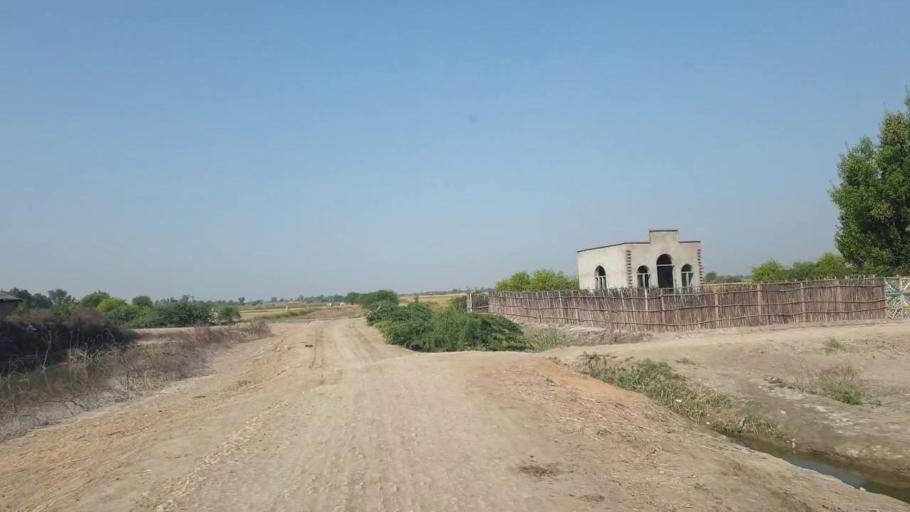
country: PK
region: Sindh
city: Badin
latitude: 24.5222
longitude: 68.7615
